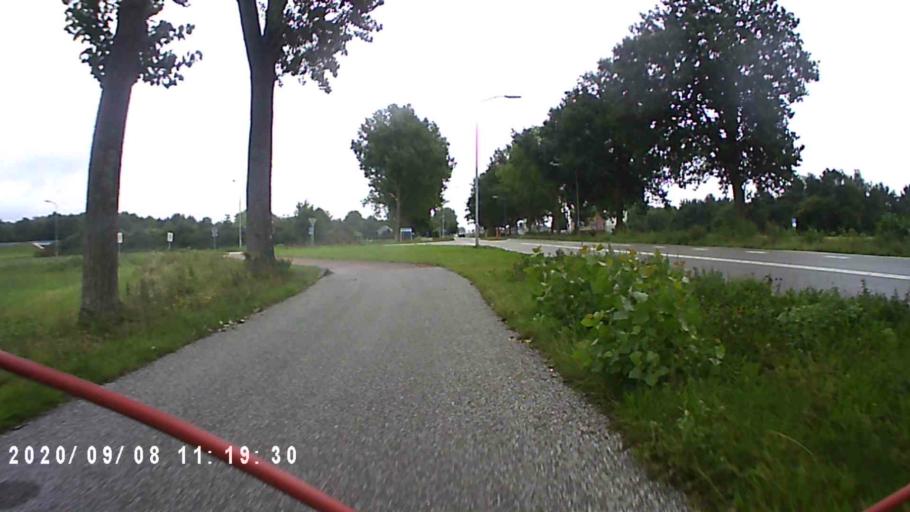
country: NL
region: Groningen
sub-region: Gemeente Hoogezand-Sappemeer
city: Hoogezand
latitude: 53.1686
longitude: 6.7501
